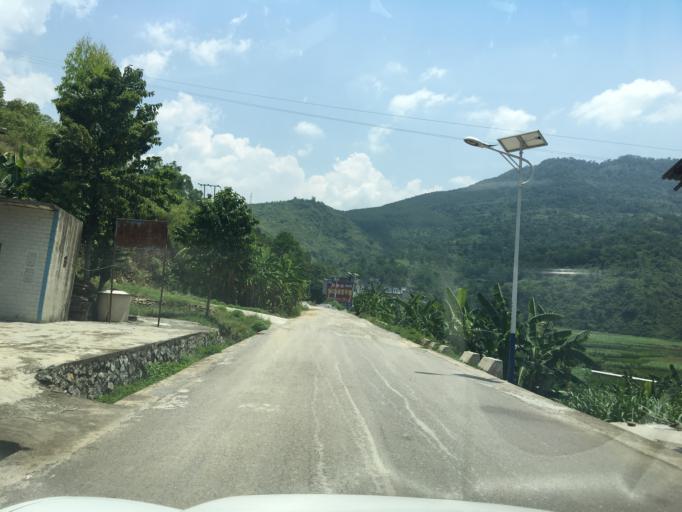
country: CN
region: Guangxi Zhuangzu Zizhiqu
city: Xinzhou
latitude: 24.9090
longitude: 105.4676
